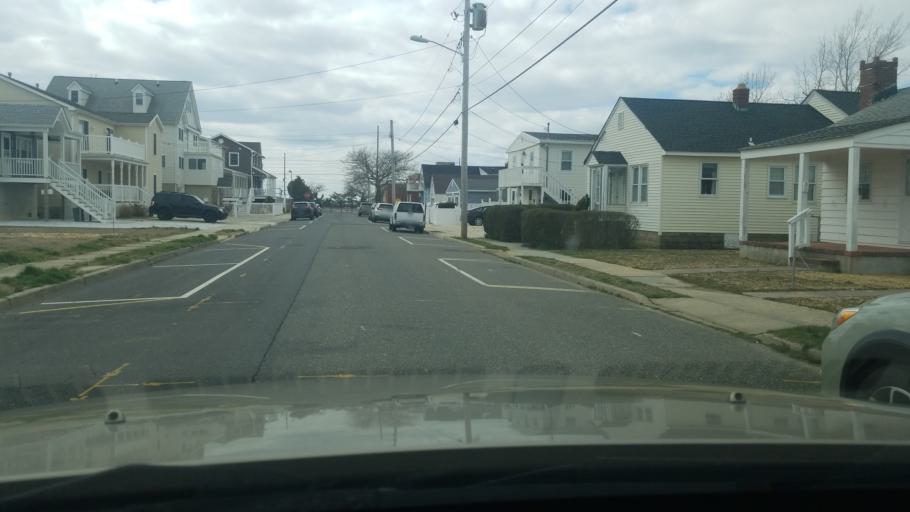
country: US
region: New Jersey
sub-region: Ocean County
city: Seaside Heights
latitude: 39.9458
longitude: -74.0765
